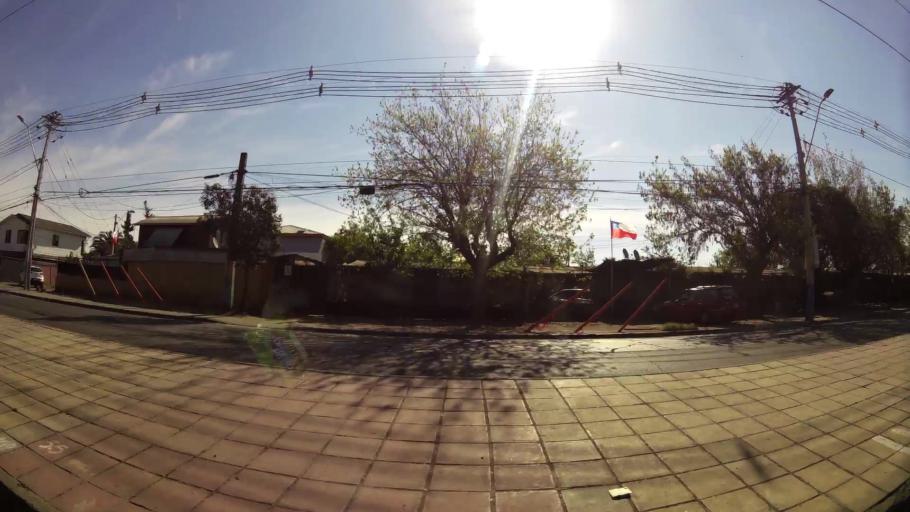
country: CL
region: Santiago Metropolitan
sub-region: Provincia de Santiago
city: Villa Presidente Frei, Nunoa, Santiago, Chile
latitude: -33.4683
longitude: -70.5677
